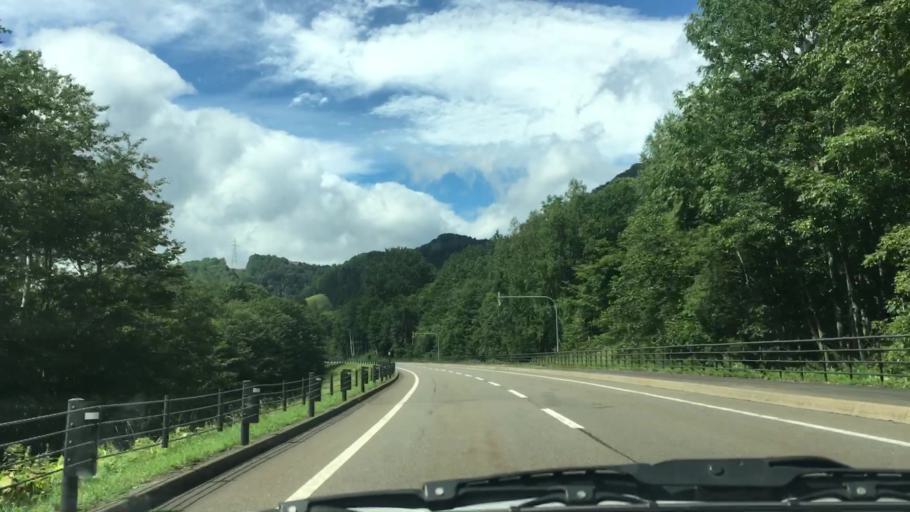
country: JP
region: Hokkaido
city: Otofuke
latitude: 43.3663
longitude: 143.2341
